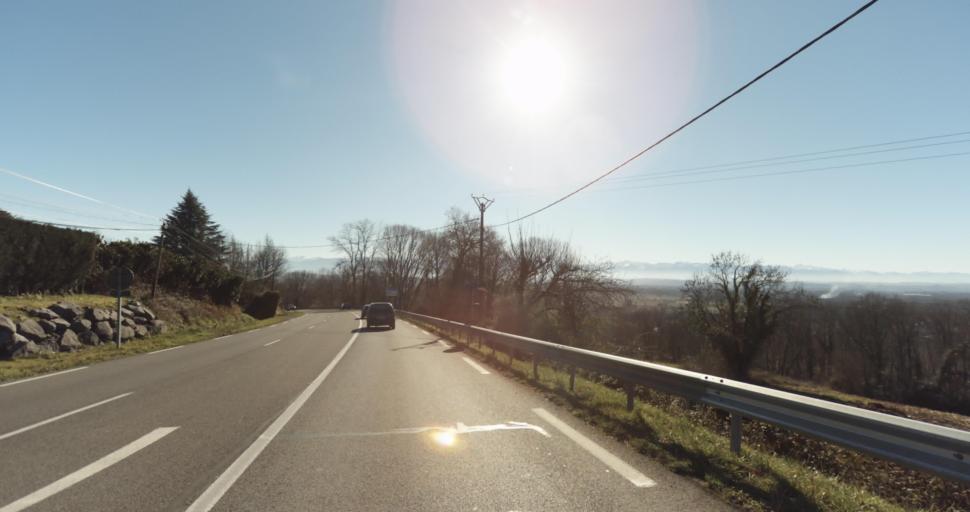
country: FR
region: Aquitaine
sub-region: Departement des Pyrenees-Atlantiques
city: Morlaas
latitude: 43.3340
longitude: -0.2785
